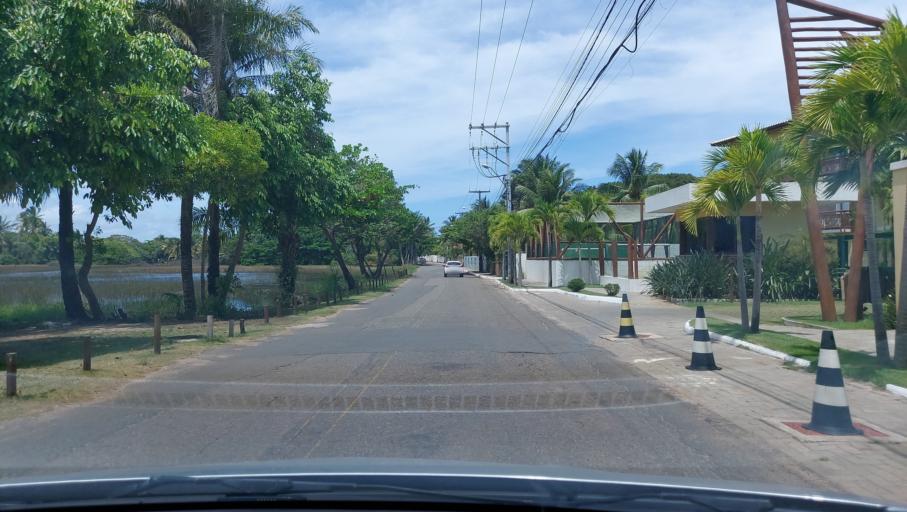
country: BR
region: Bahia
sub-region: Mata De Sao Joao
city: Mata de Sao Joao
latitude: -12.6189
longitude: -38.0457
